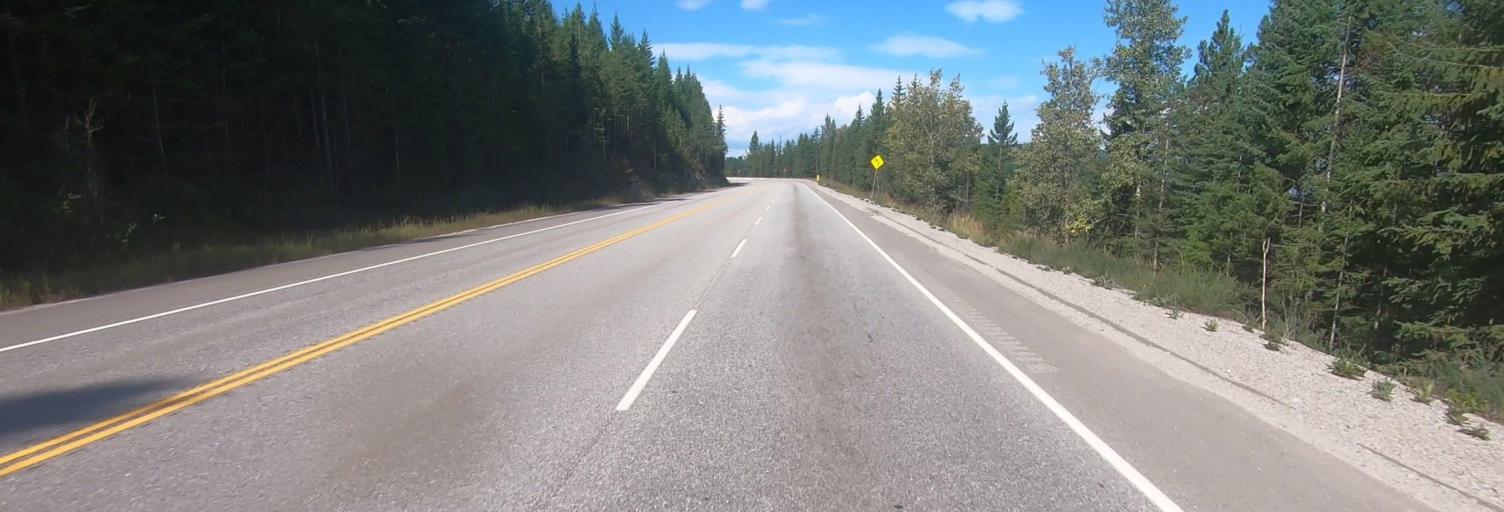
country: CA
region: British Columbia
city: Golden
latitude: 51.4955
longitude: -117.2185
